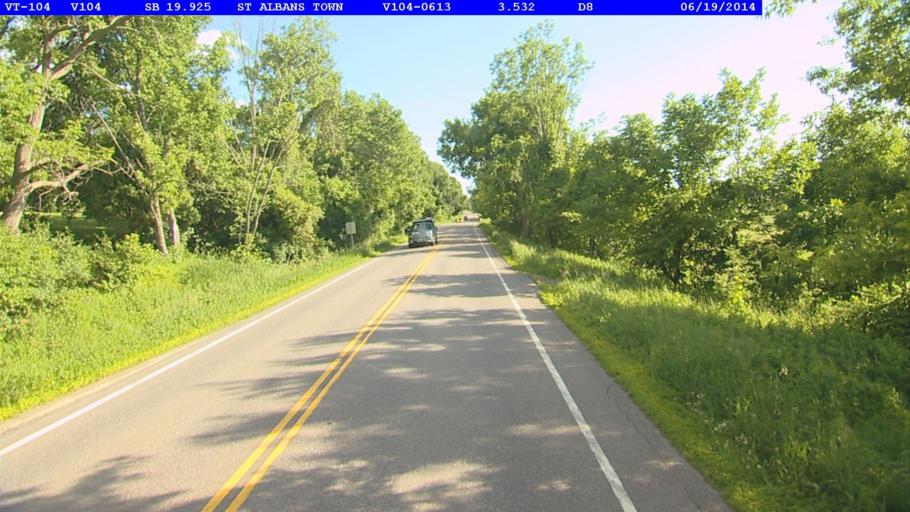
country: US
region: Vermont
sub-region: Franklin County
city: Saint Albans
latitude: 44.8211
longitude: -73.0578
